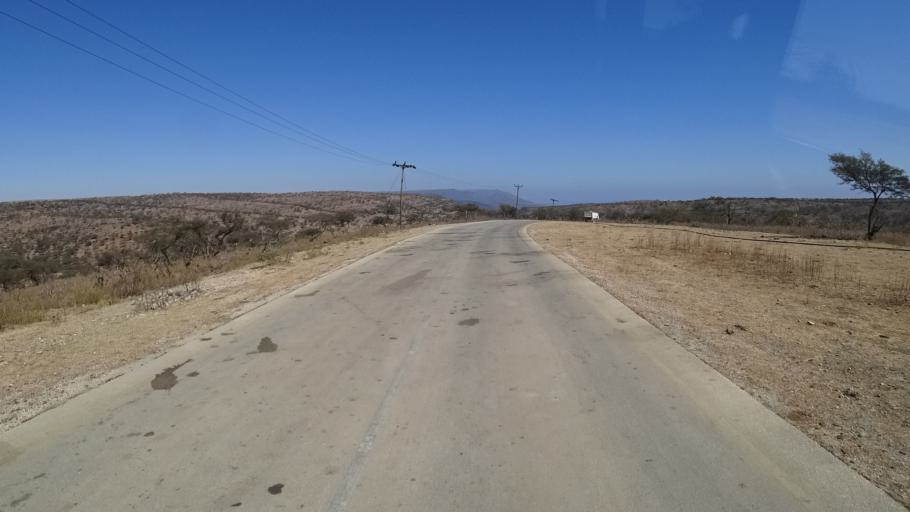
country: YE
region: Al Mahrah
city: Hawf
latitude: 16.7907
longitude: 53.3248
